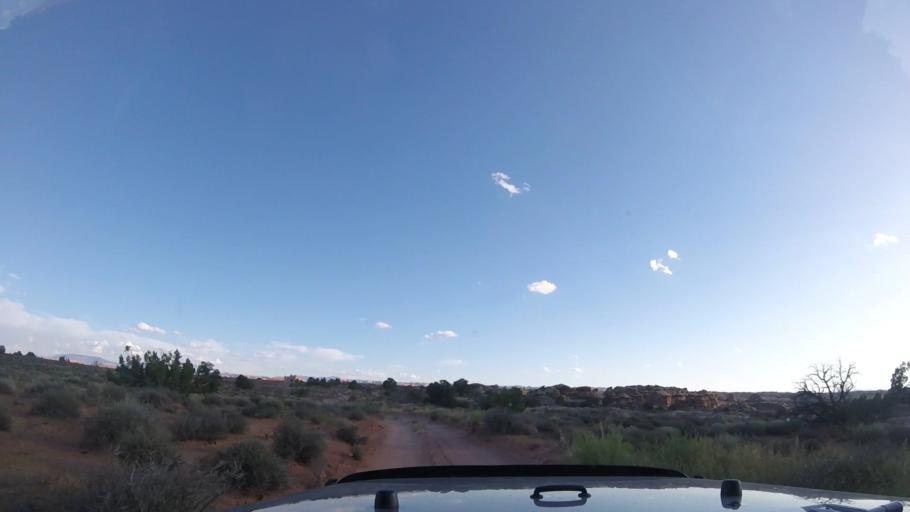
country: US
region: Utah
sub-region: Grand County
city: Moab
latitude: 38.2009
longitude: -109.7830
